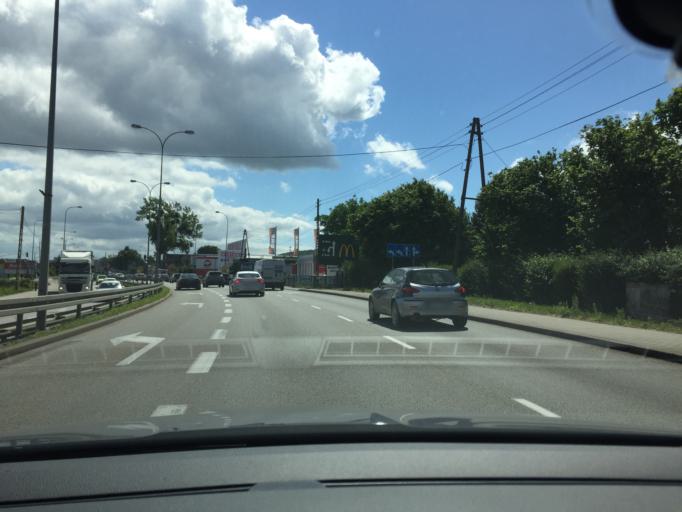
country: PL
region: Pomeranian Voivodeship
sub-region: Powiat wejherowski
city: Reda
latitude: 54.5849
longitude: 18.3633
